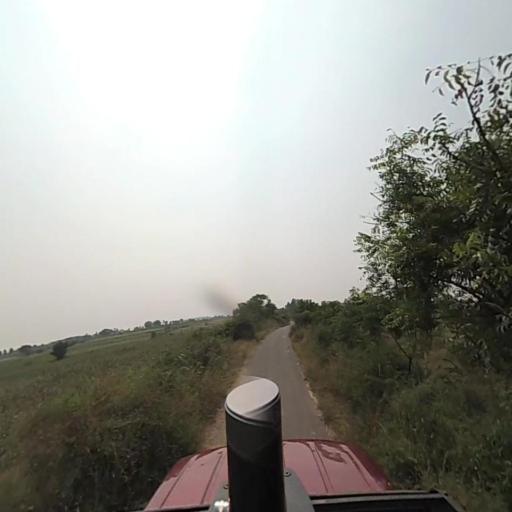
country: IN
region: Telangana
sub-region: Nalgonda
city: Nalgonda
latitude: 17.2044
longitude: 79.1451
